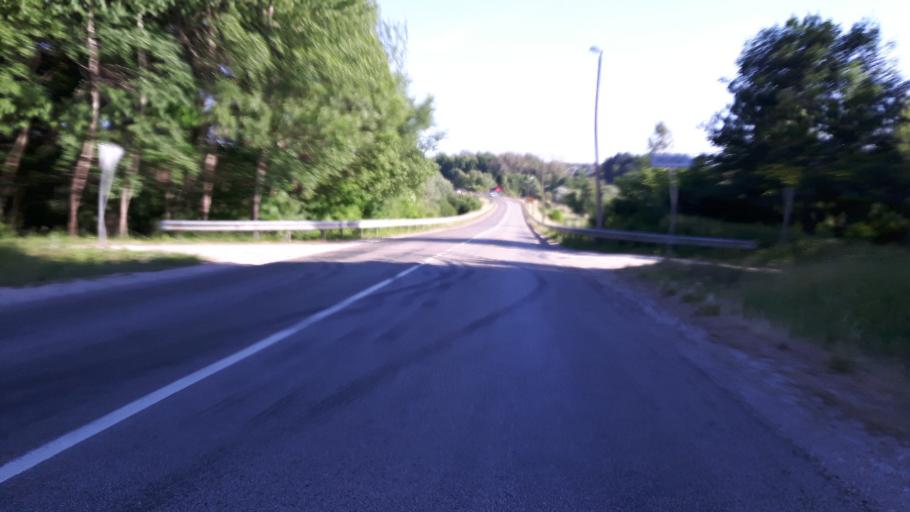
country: LV
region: Talsu Rajons
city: Stende
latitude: 57.0744
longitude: 22.2913
